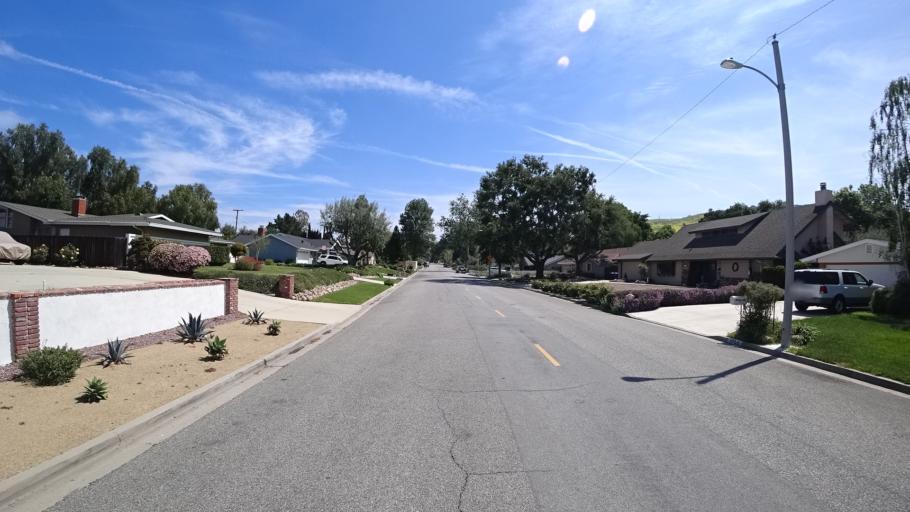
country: US
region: California
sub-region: Ventura County
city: Thousand Oaks
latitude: 34.2031
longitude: -118.8454
